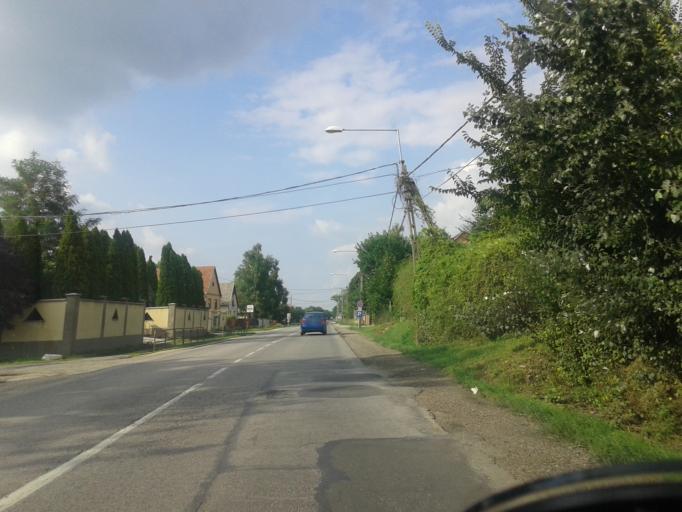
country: HU
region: Bacs-Kiskun
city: Solt
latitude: 46.8090
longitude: 19.0052
